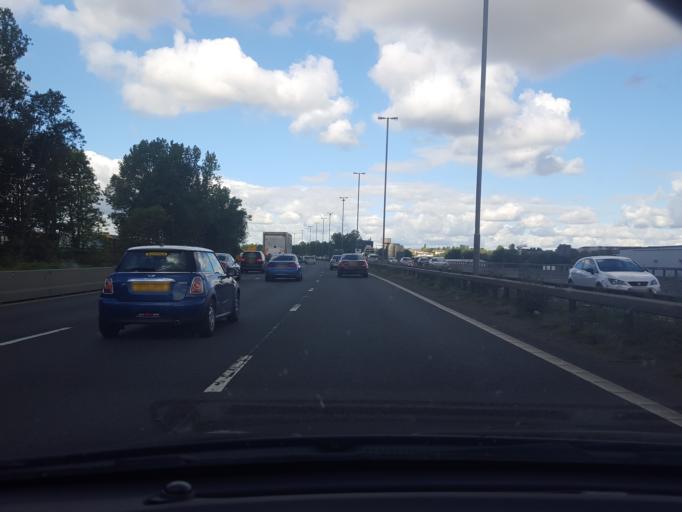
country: GB
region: Scotland
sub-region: South Lanarkshire
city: Bothwell
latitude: 55.8160
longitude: -4.0651
